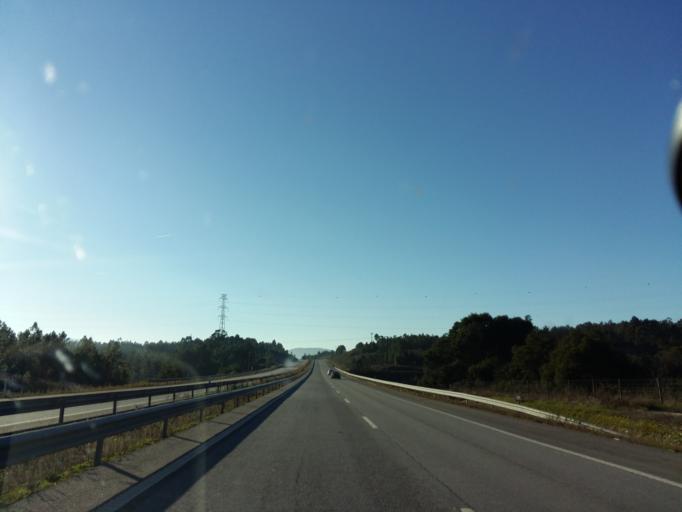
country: ES
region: Extremadura
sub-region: Provincia de Caceres
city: Cedillo
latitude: 39.7332
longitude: -7.6652
